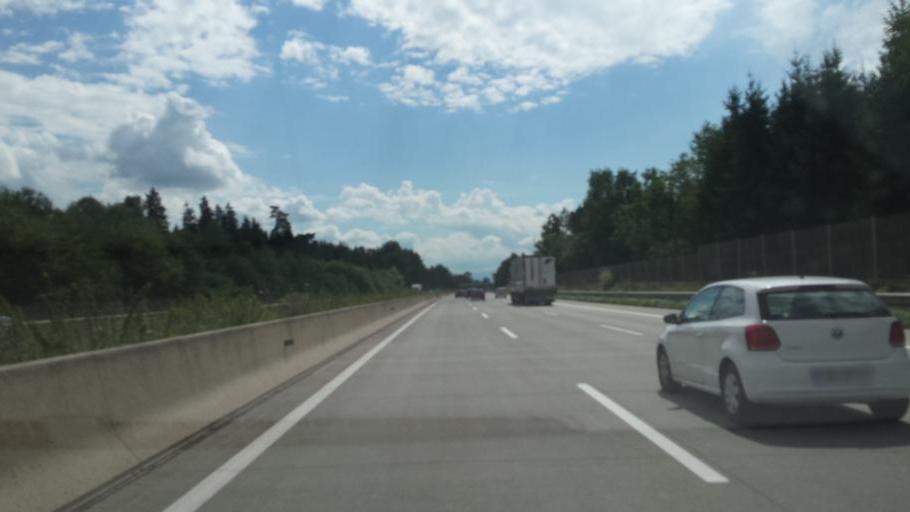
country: AT
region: Upper Austria
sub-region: Wels-Land
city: Sattledt
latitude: 48.1104
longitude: 14.0978
